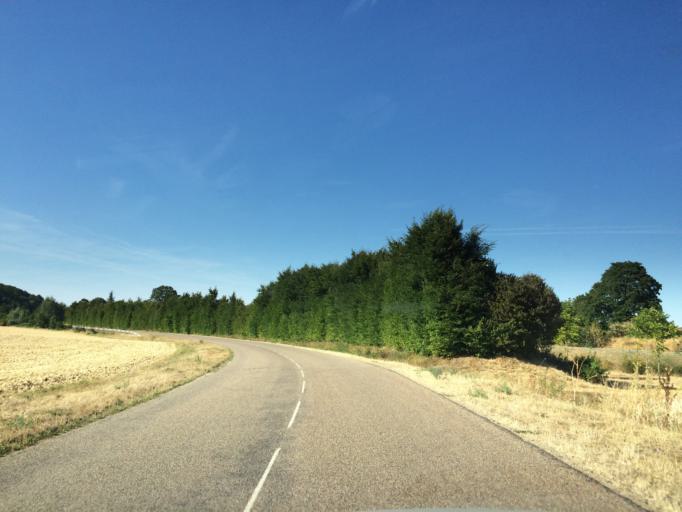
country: FR
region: Bourgogne
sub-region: Departement de l'Yonne
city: Cheny
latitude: 47.9184
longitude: 3.5129
